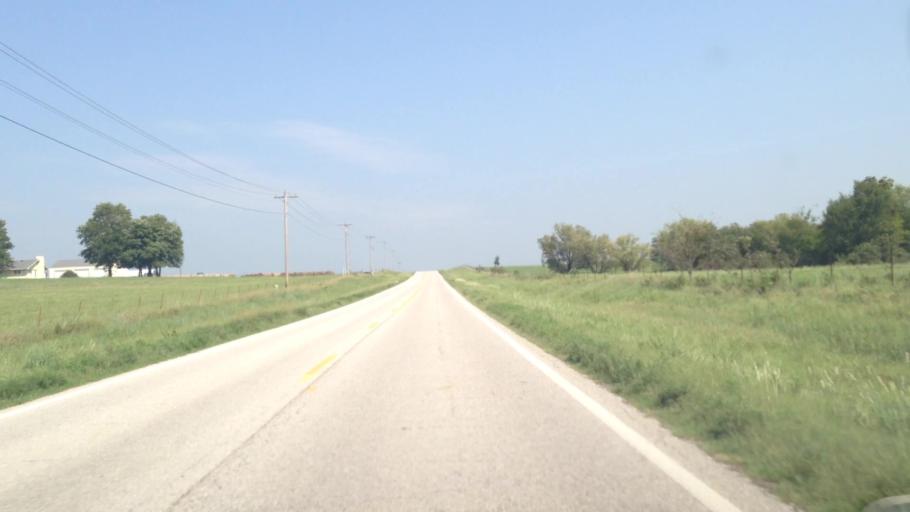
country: US
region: Oklahoma
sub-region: Craig County
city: Vinita
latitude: 36.7367
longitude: -95.1435
